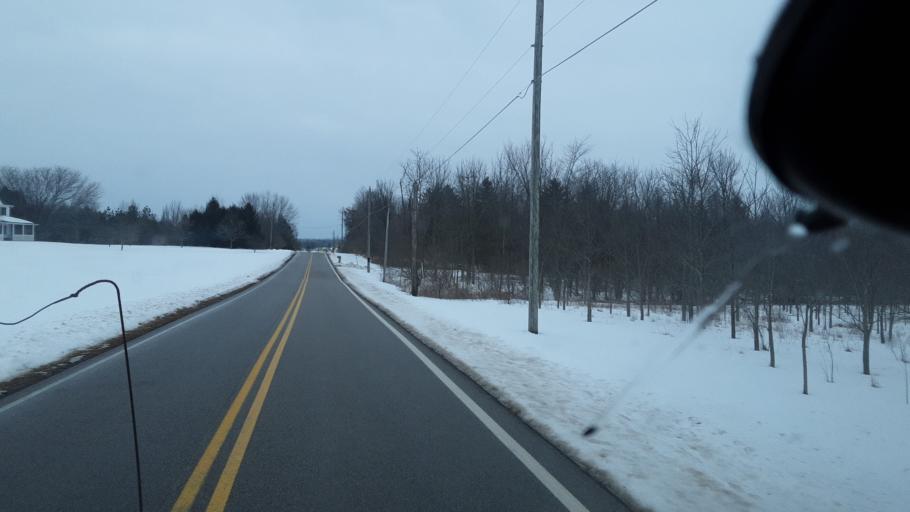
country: US
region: Ohio
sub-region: Madison County
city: Plain City
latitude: 40.1404
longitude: -83.3263
